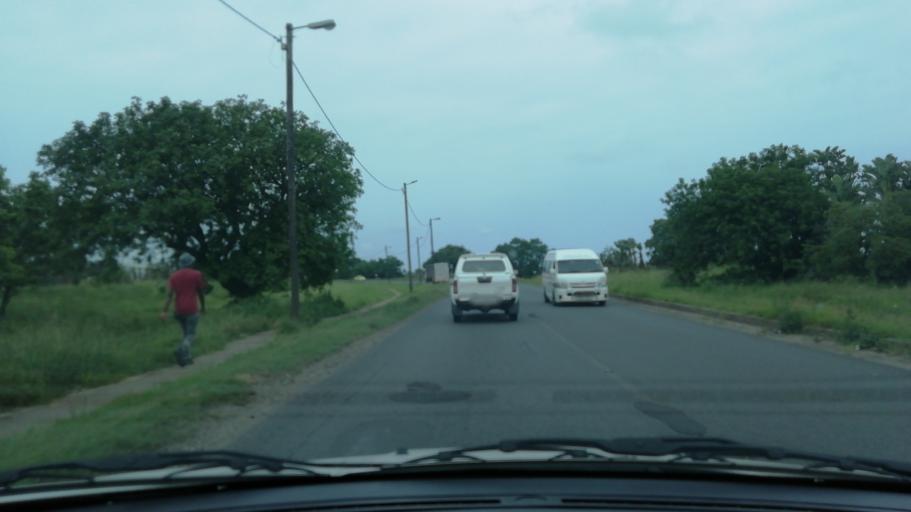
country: ZA
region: KwaZulu-Natal
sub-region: uThungulu District Municipality
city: Richards Bay
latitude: -28.7627
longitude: 32.0407
